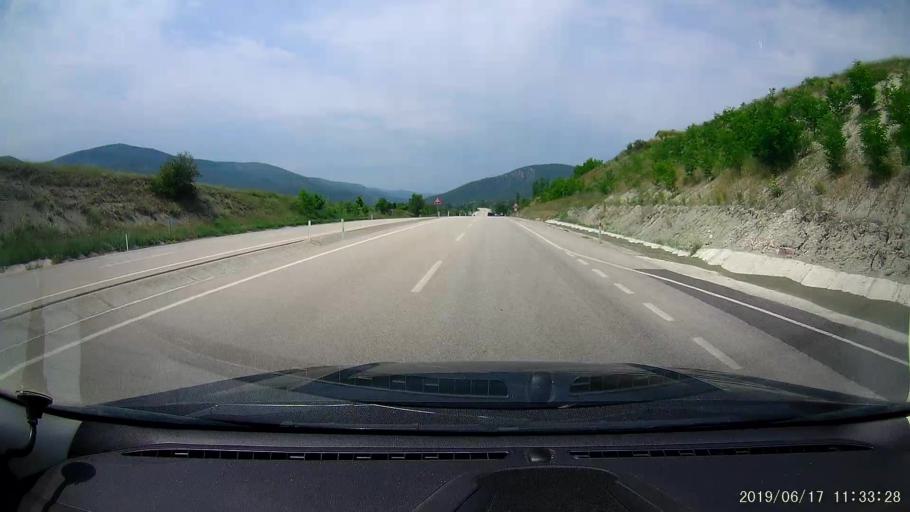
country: TR
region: Cankiri
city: Beloren
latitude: 40.8787
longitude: 33.5142
